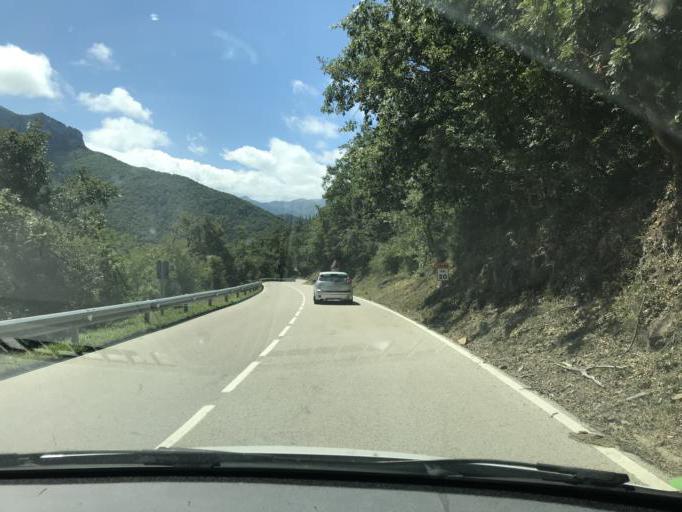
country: ES
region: Cantabria
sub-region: Provincia de Cantabria
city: Cabezon de Liebana
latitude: 43.0767
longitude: -4.4831
